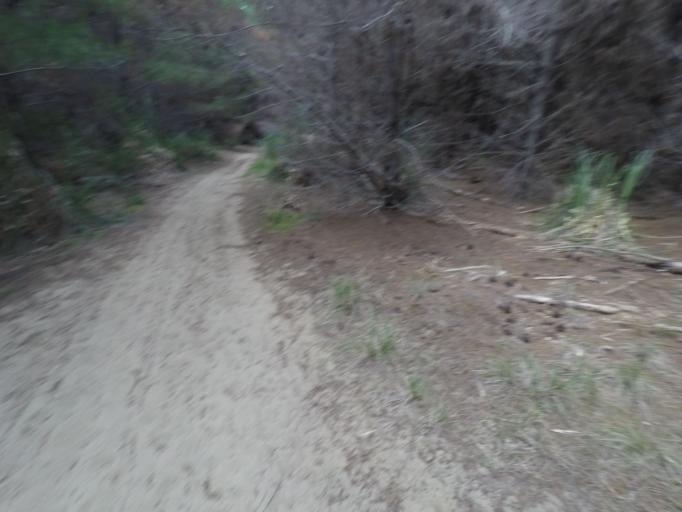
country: NZ
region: Auckland
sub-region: Auckland
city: Parakai
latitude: -36.6014
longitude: 174.2739
